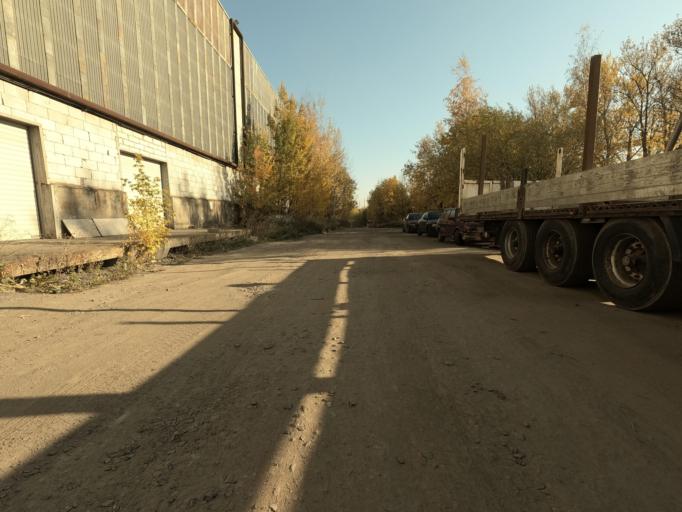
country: RU
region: Leningrad
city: Rybatskoye
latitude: 59.8416
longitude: 30.4757
